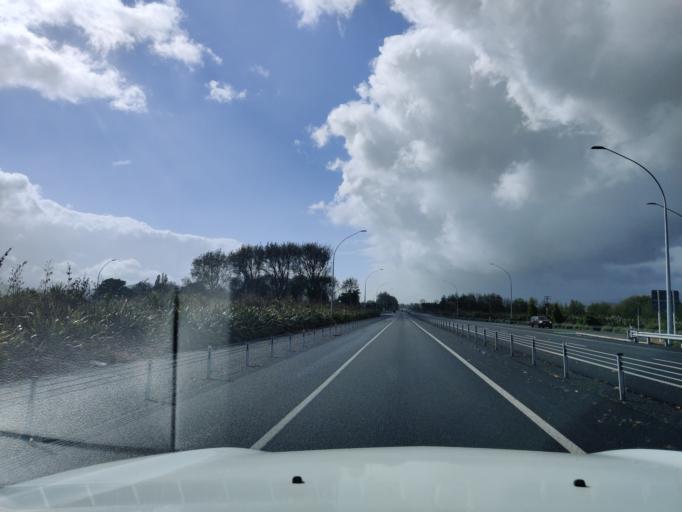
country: NZ
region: Waikato
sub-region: Waipa District
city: Cambridge
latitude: -37.8956
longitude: 175.5059
